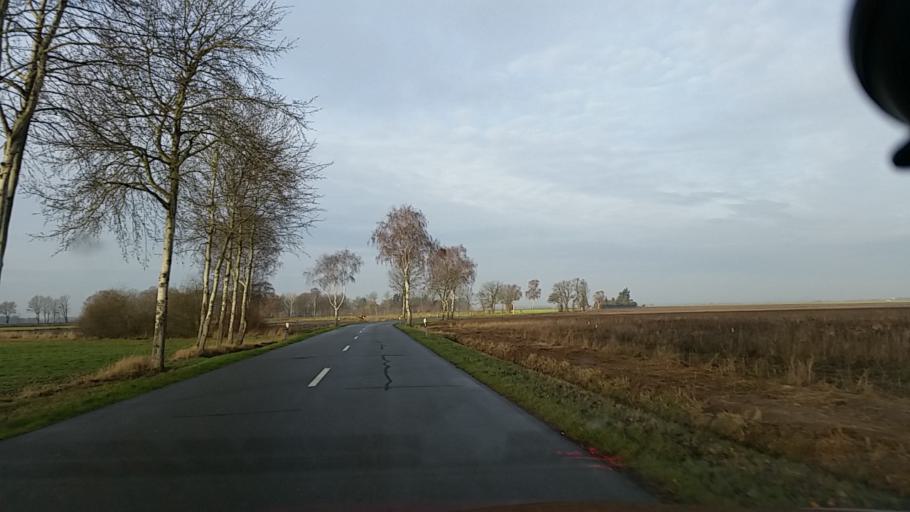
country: DE
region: Lower Saxony
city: Luder
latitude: 52.7997
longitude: 10.7004
